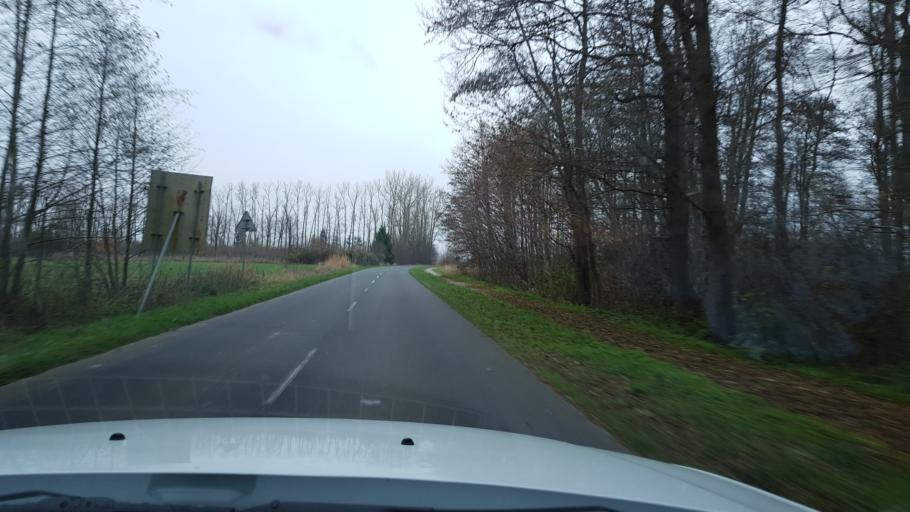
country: PL
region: West Pomeranian Voivodeship
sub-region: Powiat kamienski
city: Kamien Pomorski
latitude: 53.9510
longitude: 14.6804
